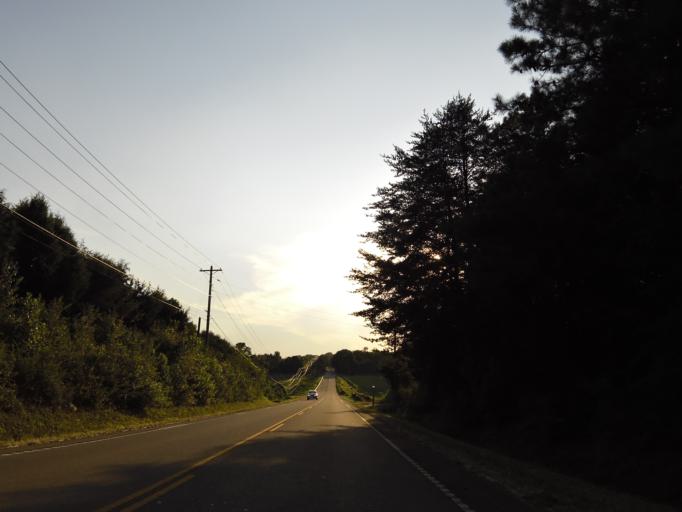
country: US
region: Tennessee
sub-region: McMinn County
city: Athens
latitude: 35.4254
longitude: -84.5548
